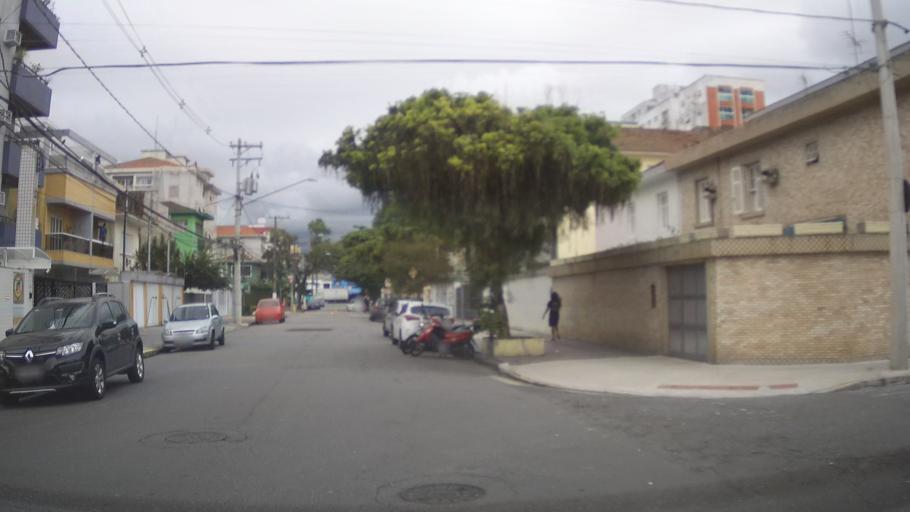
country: BR
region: Sao Paulo
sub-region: Santos
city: Santos
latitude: -23.9712
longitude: -46.3123
